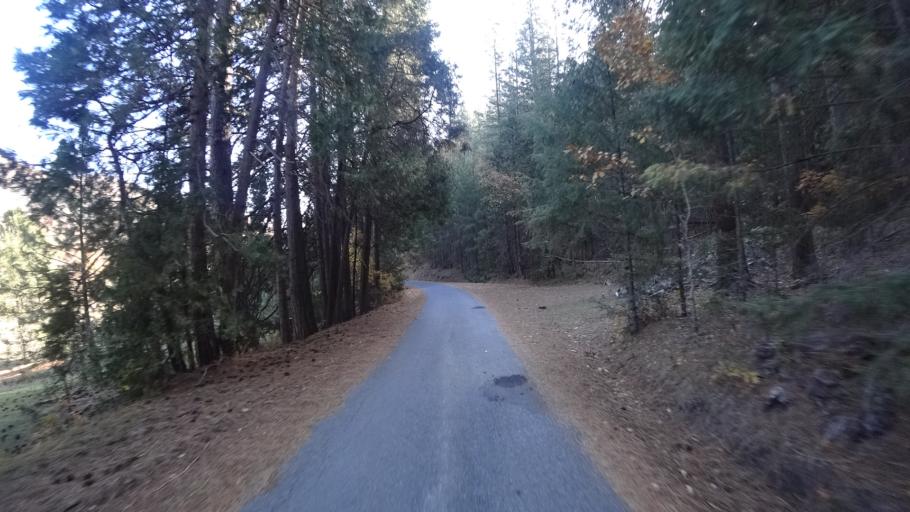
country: US
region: California
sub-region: Siskiyou County
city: Yreka
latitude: 41.8402
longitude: -122.8774
